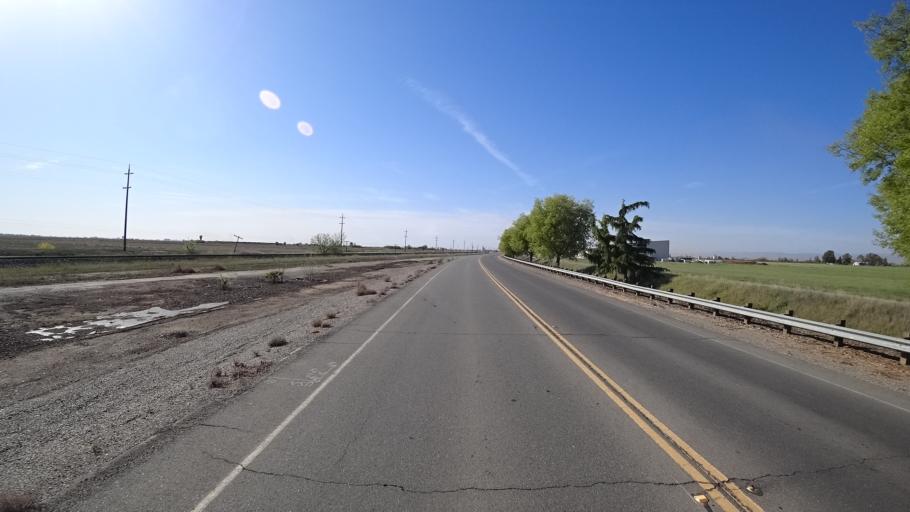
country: US
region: California
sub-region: Glenn County
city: Willows
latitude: 39.5068
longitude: -122.1935
